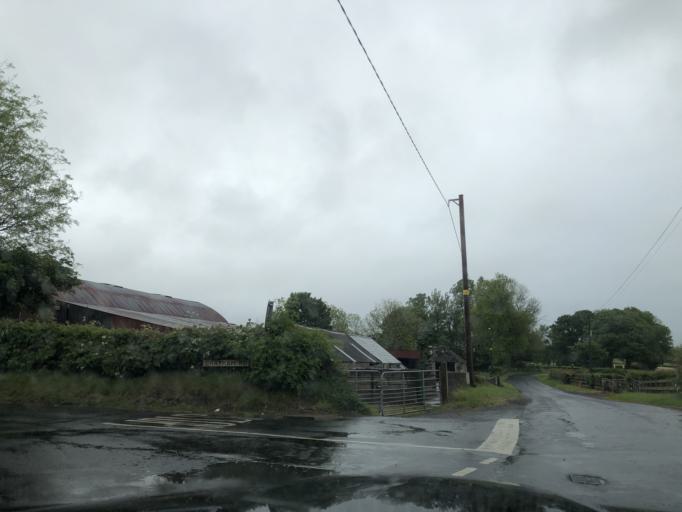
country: GB
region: Northern Ireland
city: Dunloy
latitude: 55.1343
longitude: -6.3677
